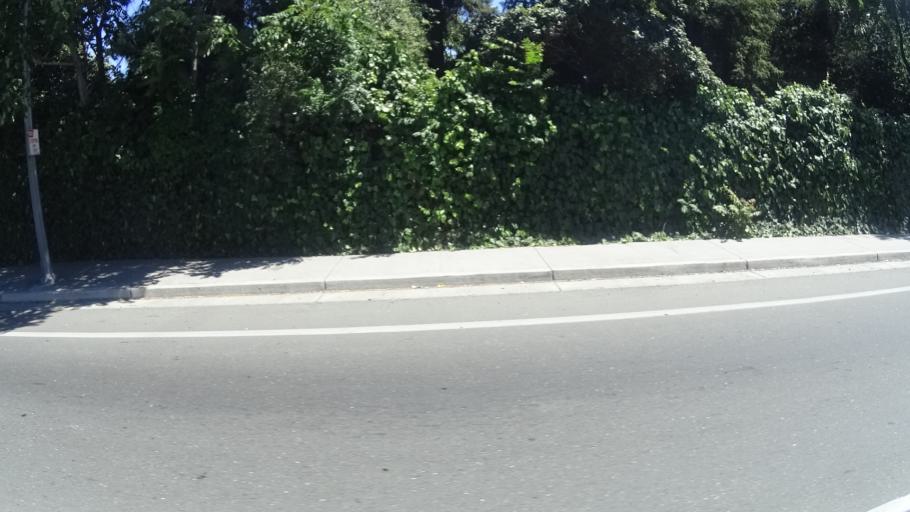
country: US
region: California
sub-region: Santa Clara County
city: San Jose
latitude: 37.3265
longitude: -121.8636
